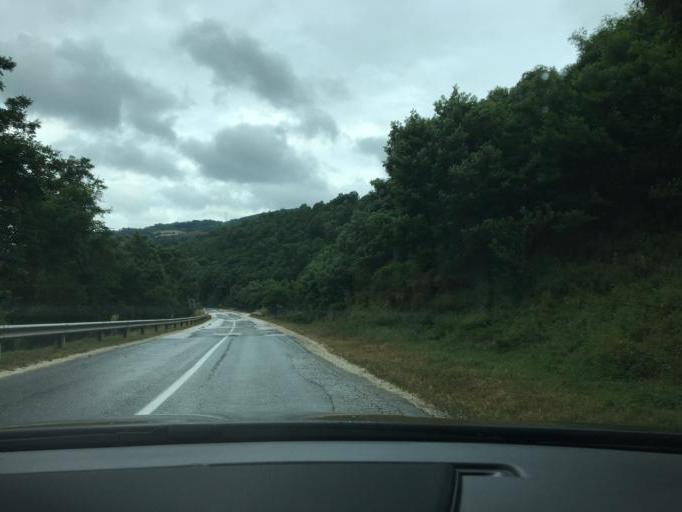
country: MK
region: Kriva Palanka
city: Kriva Palanka
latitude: 42.2232
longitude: 22.4220
